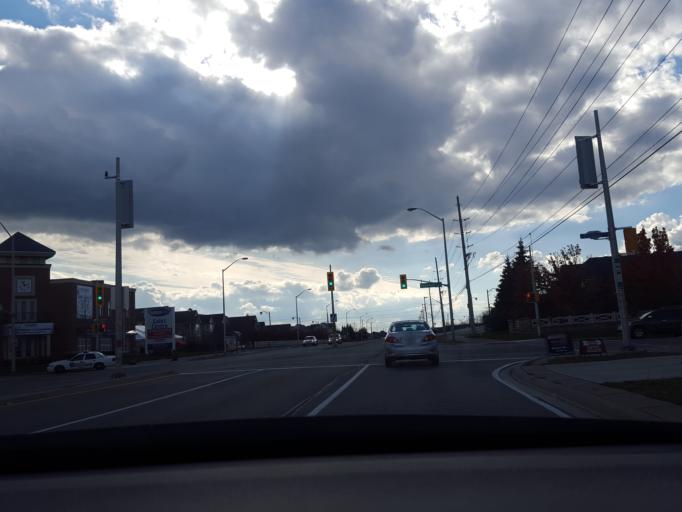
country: CA
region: Ontario
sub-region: Halton
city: Milton
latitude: 43.5284
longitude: -79.8376
